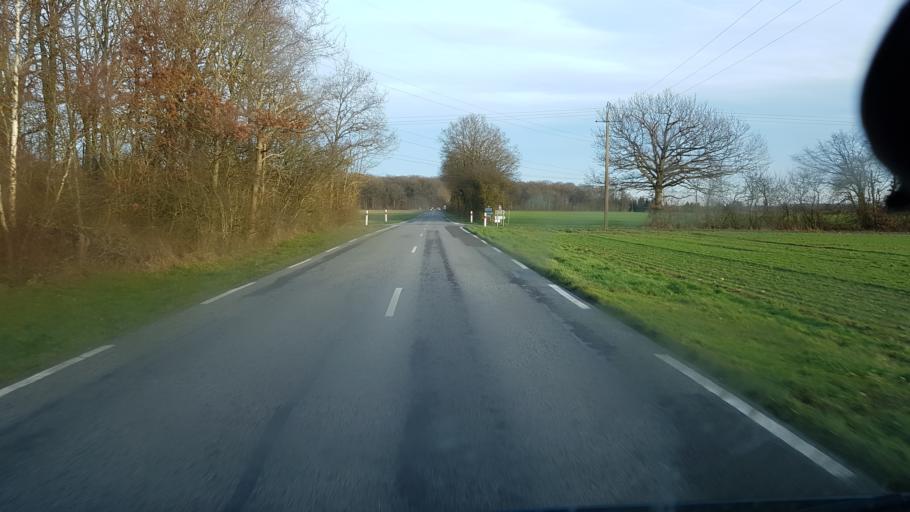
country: FR
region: Ile-de-France
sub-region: Departement des Yvelines
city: Auffargis
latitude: 48.6823
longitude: 1.8857
